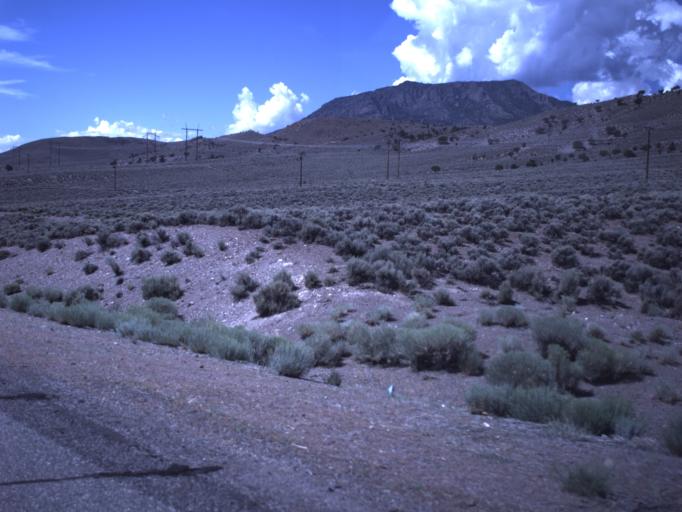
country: US
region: Utah
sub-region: Piute County
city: Junction
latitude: 38.3087
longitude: -112.2227
